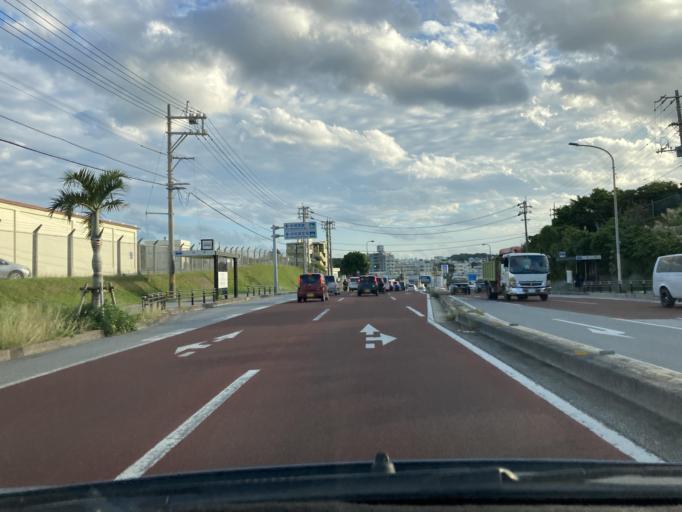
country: JP
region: Okinawa
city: Chatan
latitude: 26.2978
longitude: 127.7806
